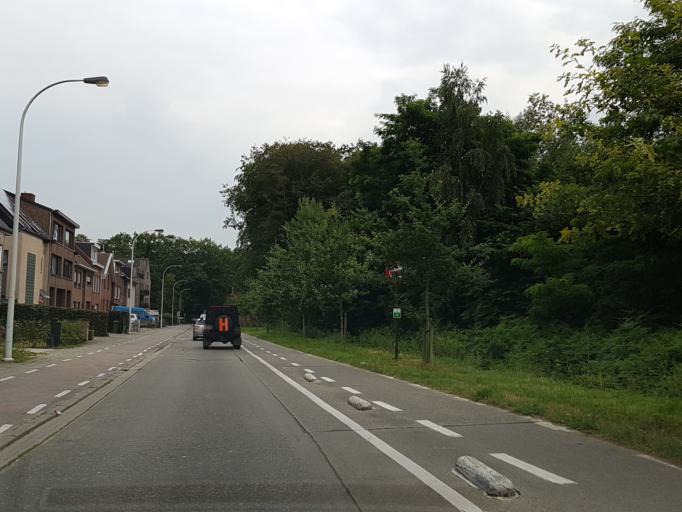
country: BE
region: Flanders
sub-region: Provincie Antwerpen
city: Schoten
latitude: 51.2450
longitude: 4.4974
